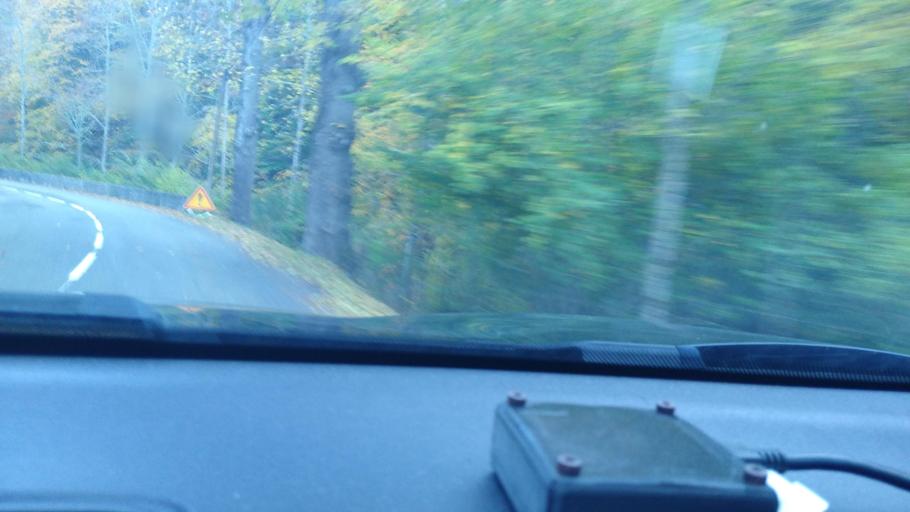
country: FR
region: Languedoc-Roussillon
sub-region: Departement de l'Aude
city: Quillan
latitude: 42.7242
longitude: 2.1161
